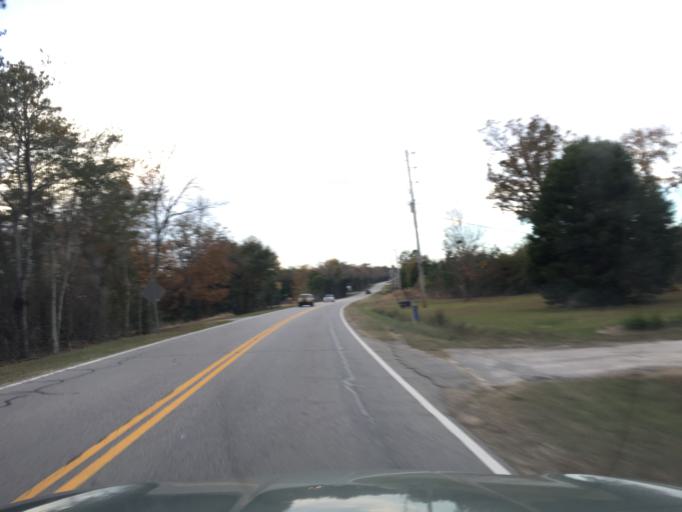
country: US
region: South Carolina
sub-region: Lexington County
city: Leesville
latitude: 33.7631
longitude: -81.3778
